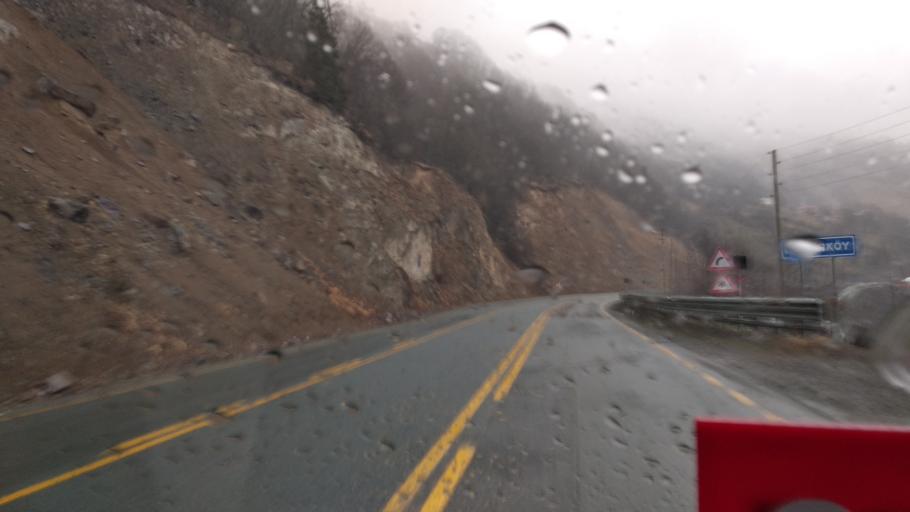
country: TR
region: Trabzon
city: Macka
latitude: 40.7060
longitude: 39.4925
